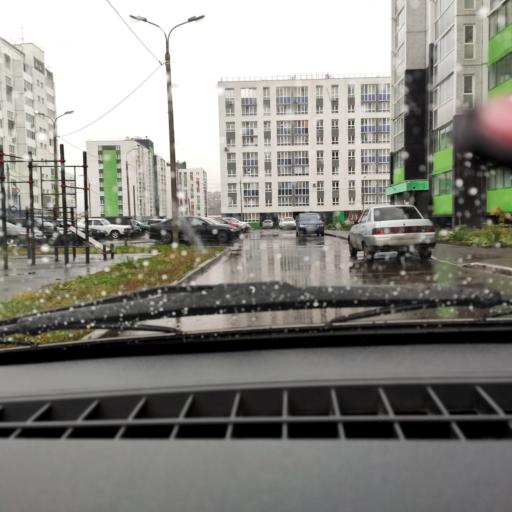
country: RU
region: Bashkortostan
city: Ufa
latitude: 54.6922
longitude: 55.9726
